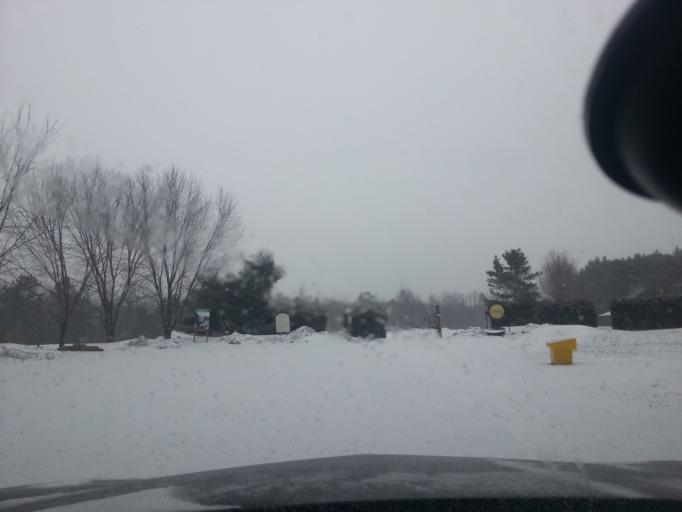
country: CA
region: Ontario
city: Carleton Place
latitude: 45.2444
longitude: -76.2582
